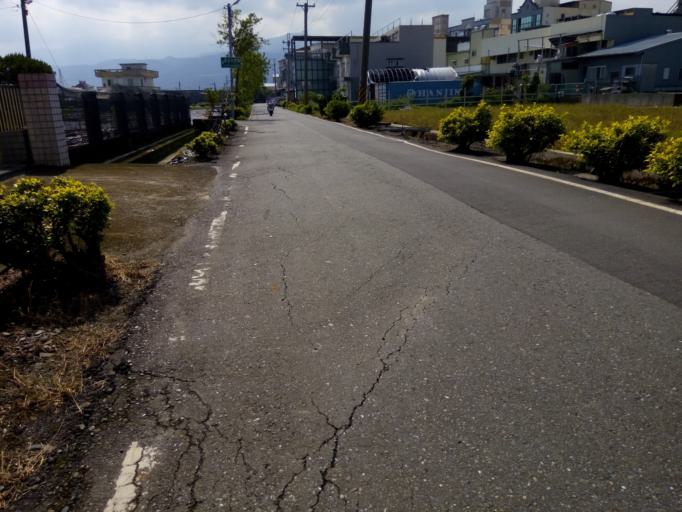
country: TW
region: Taiwan
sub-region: Yilan
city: Yilan
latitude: 24.6708
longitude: 121.7787
